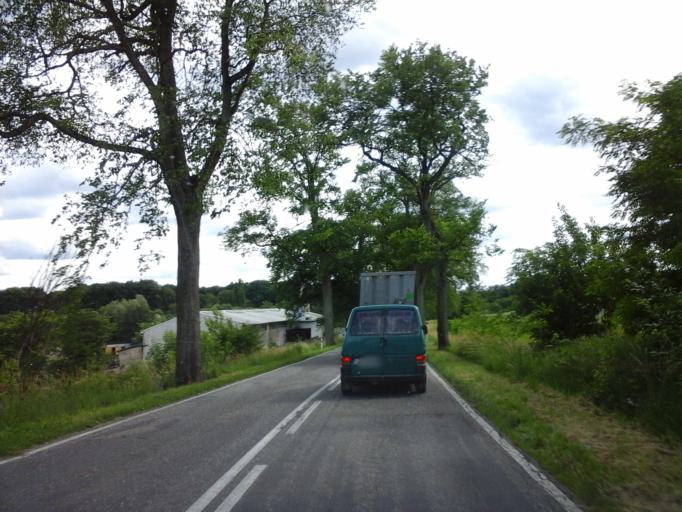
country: PL
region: West Pomeranian Voivodeship
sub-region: Powiat choszczenski
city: Recz
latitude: 53.2750
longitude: 15.5685
